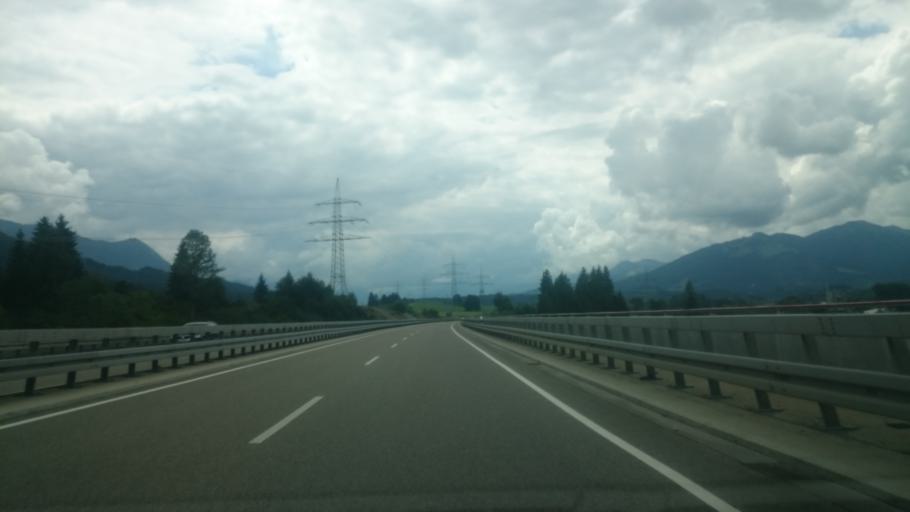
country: DE
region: Bavaria
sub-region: Swabia
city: Rettenberg
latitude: 47.6073
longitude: 10.2735
